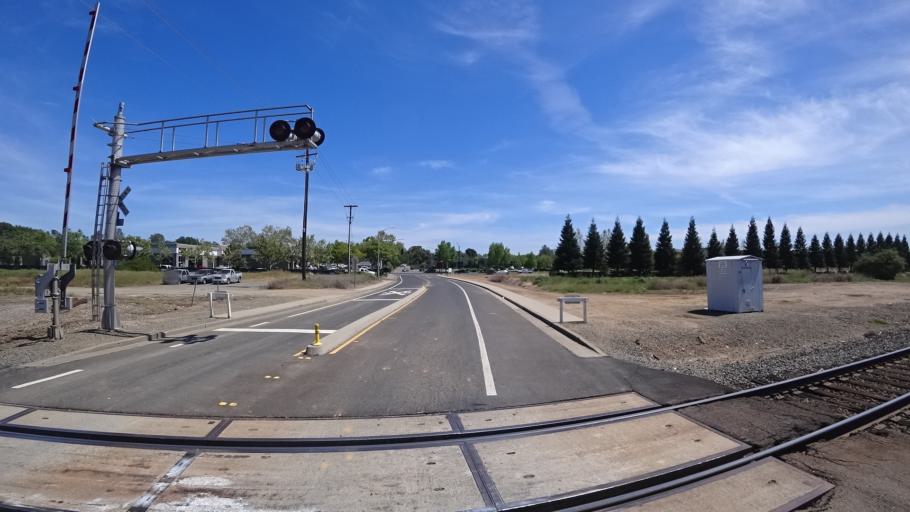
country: US
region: California
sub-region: Placer County
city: Rocklin
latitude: 38.7864
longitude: -121.2410
